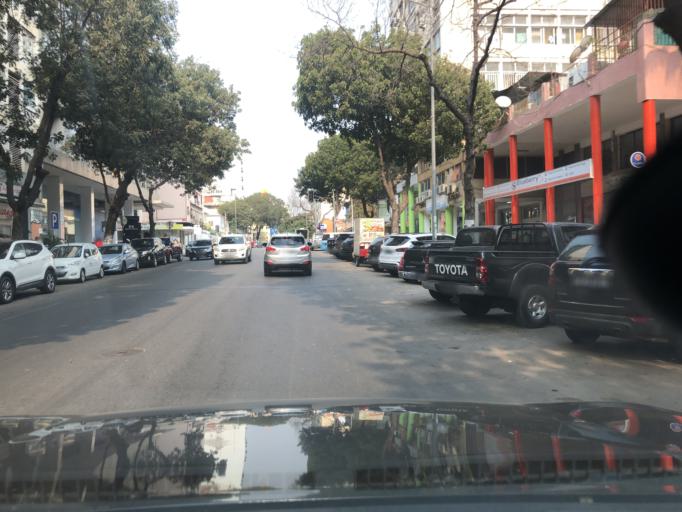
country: AO
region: Luanda
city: Luanda
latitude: -8.8192
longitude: 13.2443
